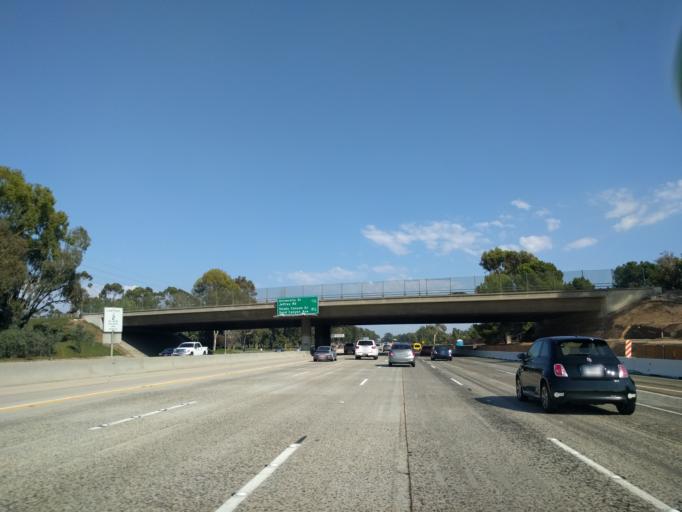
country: US
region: California
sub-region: Orange County
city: Irvine
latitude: 33.6697
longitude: -117.8238
